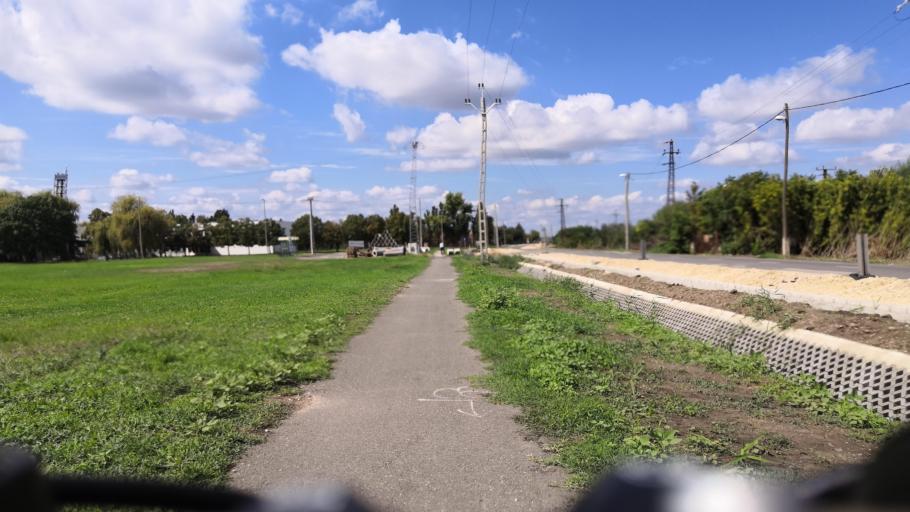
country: HU
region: Csongrad
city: Szeged
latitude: 46.2784
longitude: 20.1316
